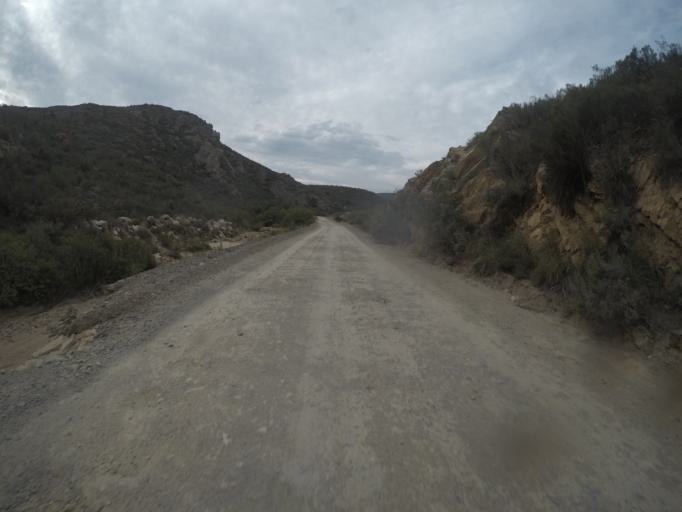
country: ZA
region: Eastern Cape
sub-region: Cacadu District Municipality
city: Willowmore
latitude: -33.5038
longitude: 23.6354
